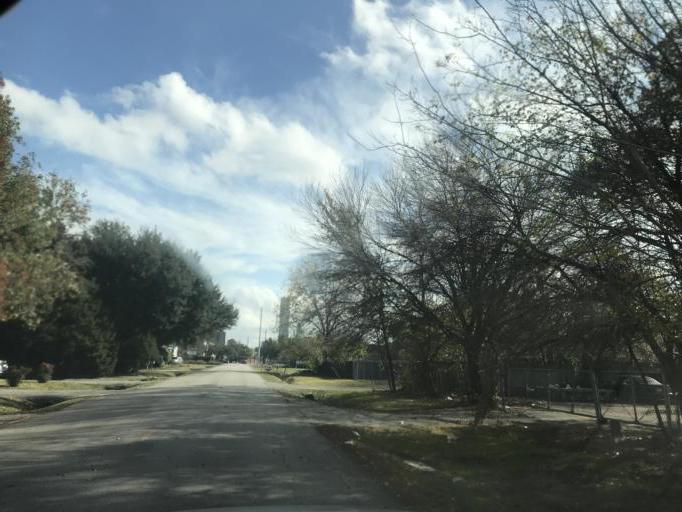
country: US
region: Texas
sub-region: Harris County
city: Bellaire
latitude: 29.7331
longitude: -95.4790
